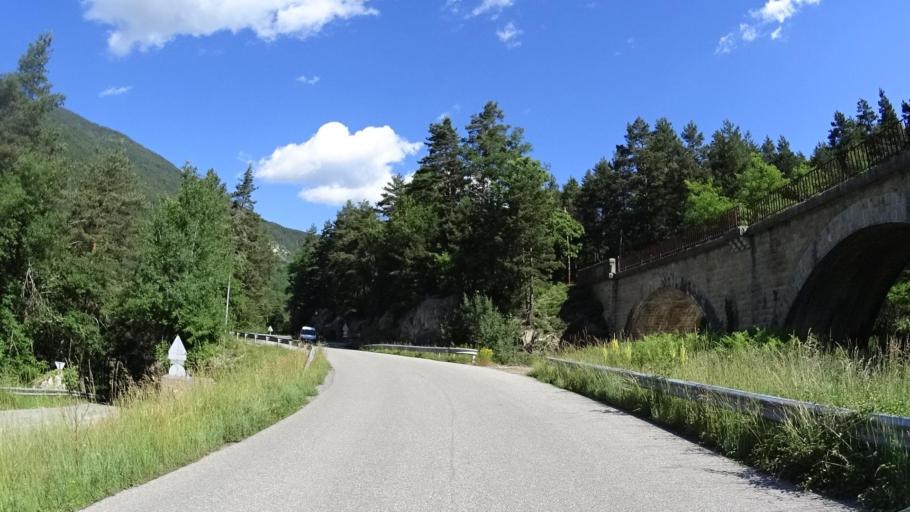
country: FR
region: Provence-Alpes-Cote d'Azur
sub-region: Departement des Alpes-de-Haute-Provence
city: Annot
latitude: 43.9907
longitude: 6.6477
